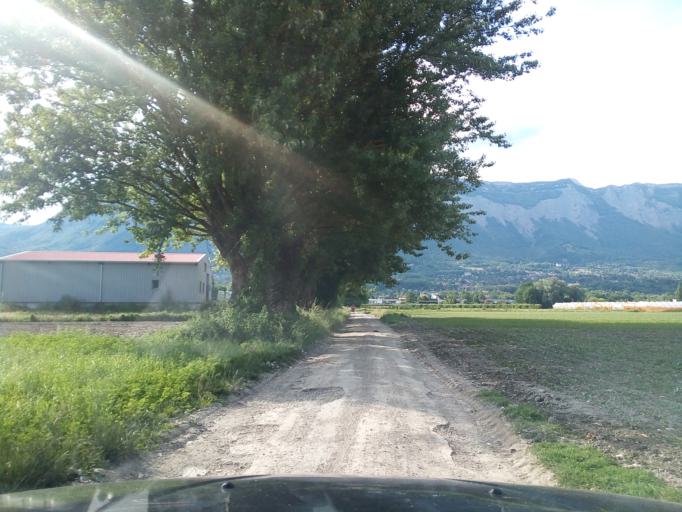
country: FR
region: Rhone-Alpes
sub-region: Departement de l'Isere
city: Montbonnot-Saint-Martin
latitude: 45.2130
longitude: 5.8198
